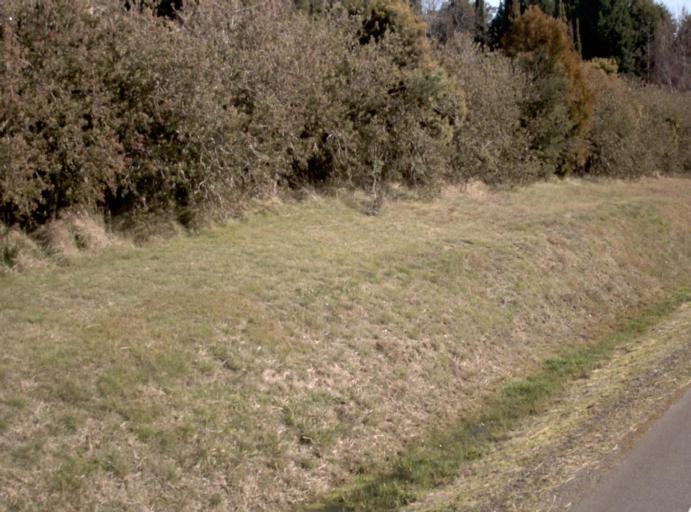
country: AU
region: Tasmania
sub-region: Launceston
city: Mayfield
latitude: -41.3200
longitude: 147.0592
